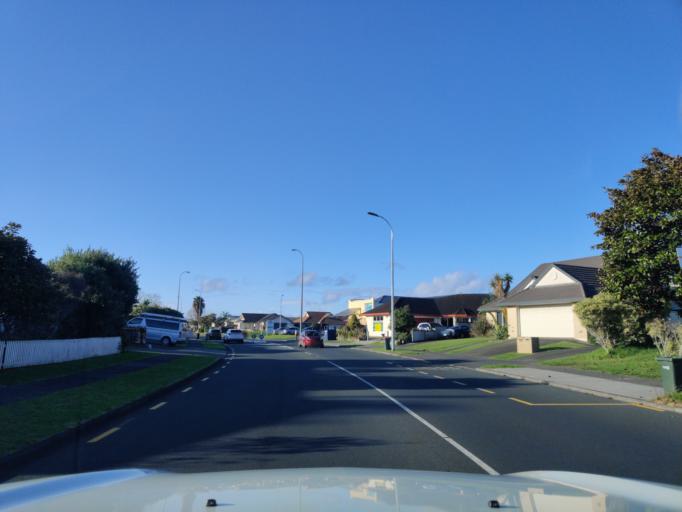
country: NZ
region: Auckland
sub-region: Auckland
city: Pakuranga
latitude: -36.9195
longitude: 174.9170
